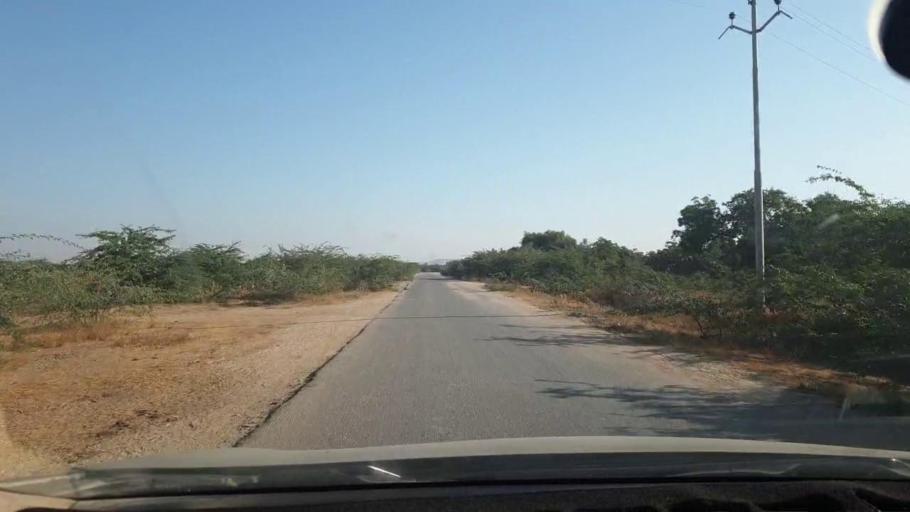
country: PK
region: Sindh
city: Malir Cantonment
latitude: 25.1684
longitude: 67.1985
